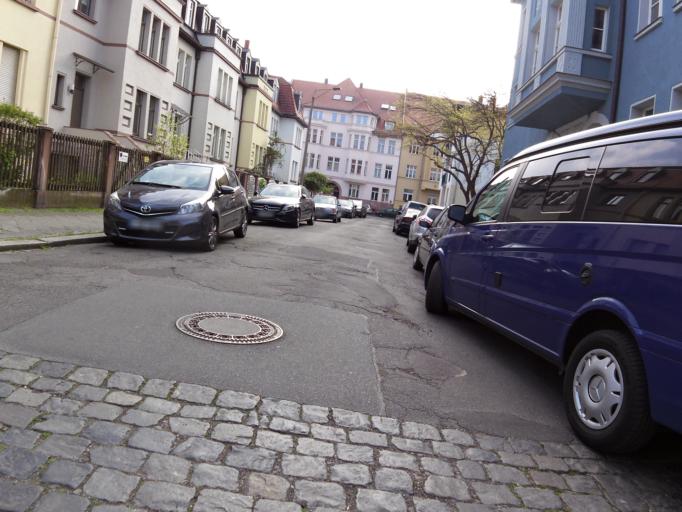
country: DE
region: Saxony
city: Leipzig
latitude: 51.3220
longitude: 12.3452
